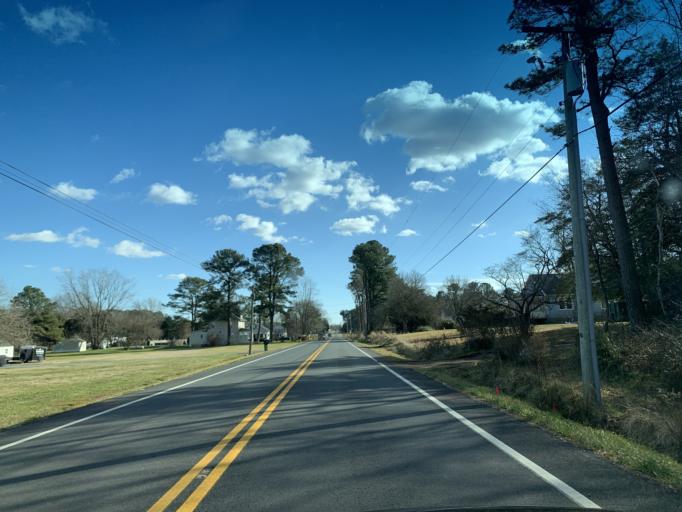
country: US
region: Maryland
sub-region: Worcester County
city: Berlin
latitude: 38.3579
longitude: -75.1980
